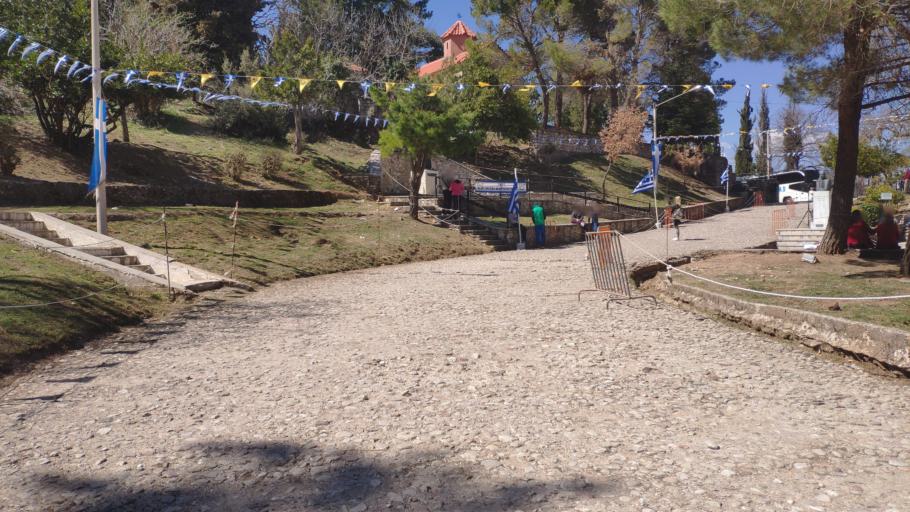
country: GR
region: West Greece
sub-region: Nomos Achaias
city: Kalavryta
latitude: 38.0121
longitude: 22.0806
